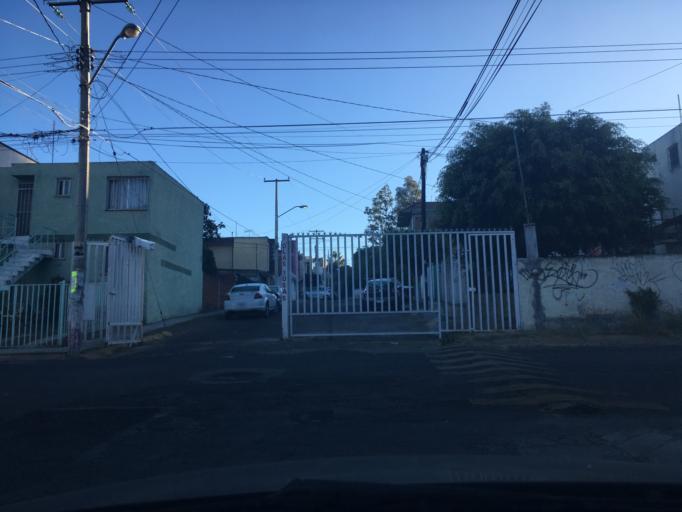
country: MX
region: Michoacan
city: Morelia
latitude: 19.6691
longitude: -101.2031
